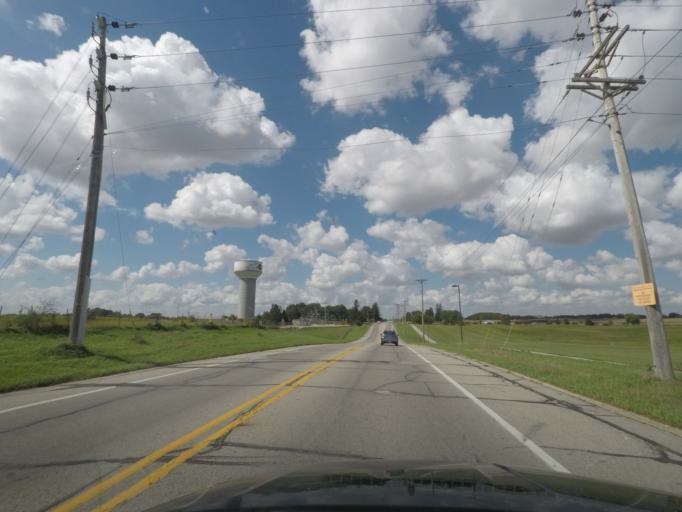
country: US
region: Iowa
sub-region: Story County
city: Ames
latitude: 42.0119
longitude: -93.6552
